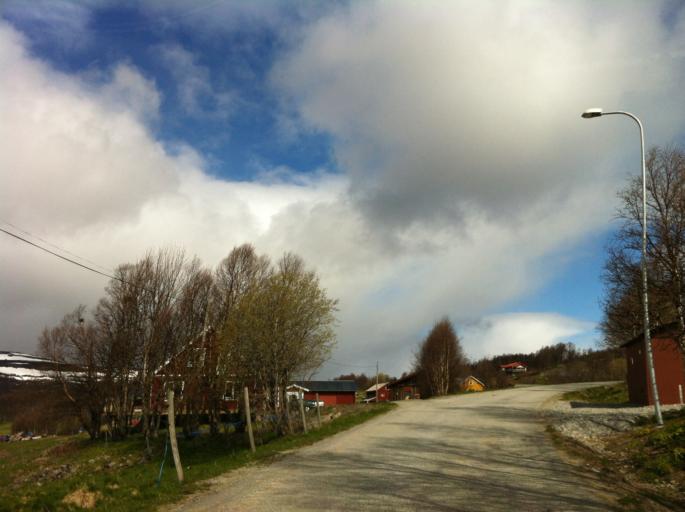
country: NO
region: Sor-Trondelag
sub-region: Tydal
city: Aas
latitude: 62.6330
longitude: 12.4447
